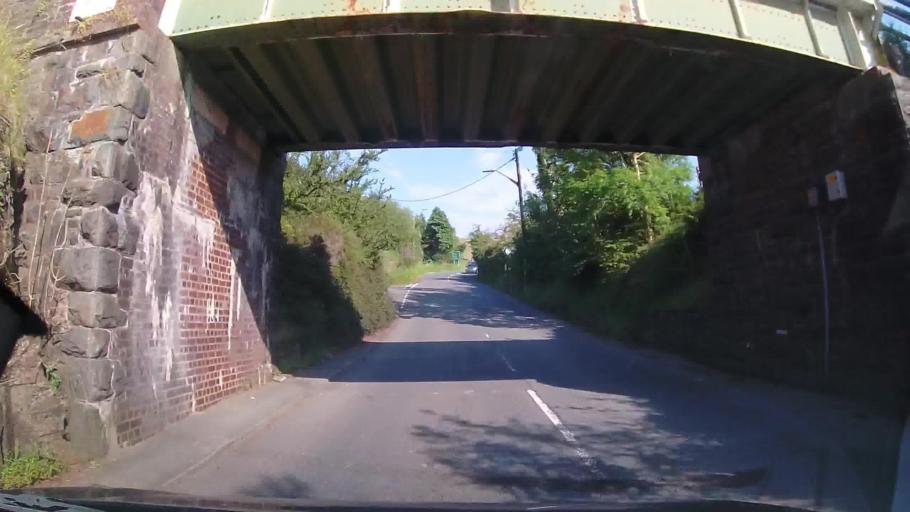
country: GB
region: Wales
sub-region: Gwynedd
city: Ffestiniog
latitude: 52.9593
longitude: -3.9309
